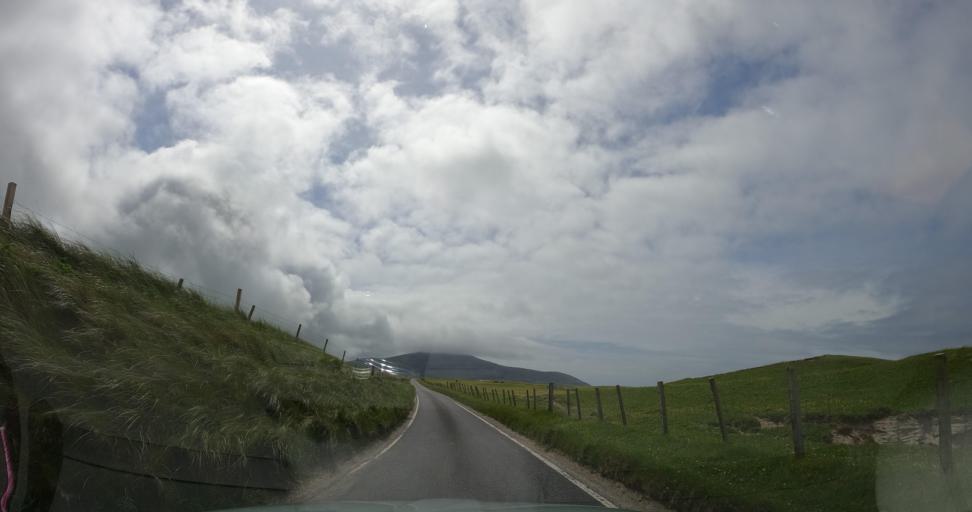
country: GB
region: Scotland
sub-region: Eilean Siar
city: Barra
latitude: 56.9986
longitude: -7.5052
